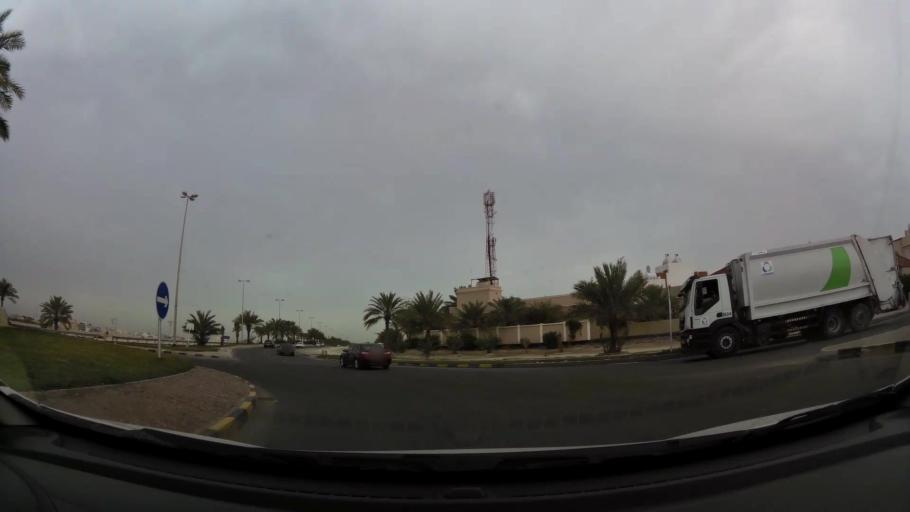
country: BH
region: Central Governorate
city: Dar Kulayb
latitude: 26.0719
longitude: 50.5079
